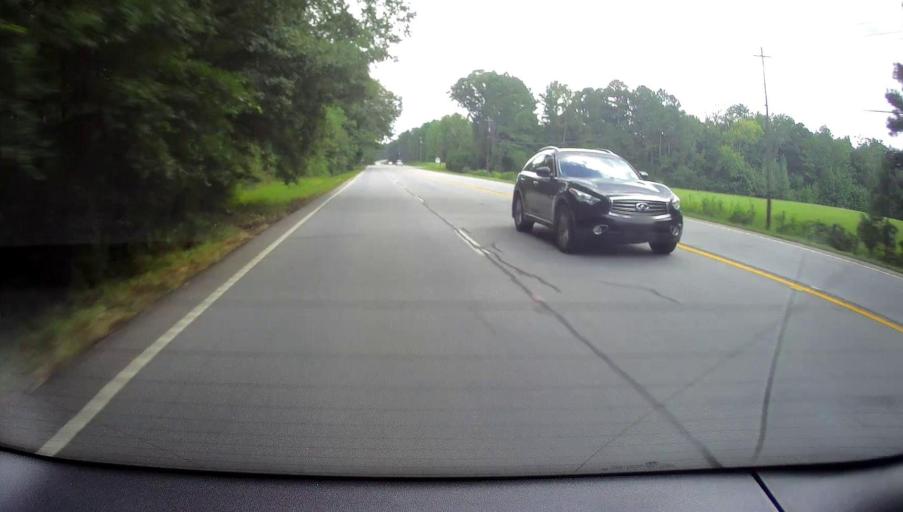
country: US
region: Georgia
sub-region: Coweta County
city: Senoia
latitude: 33.1888
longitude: -84.5804
